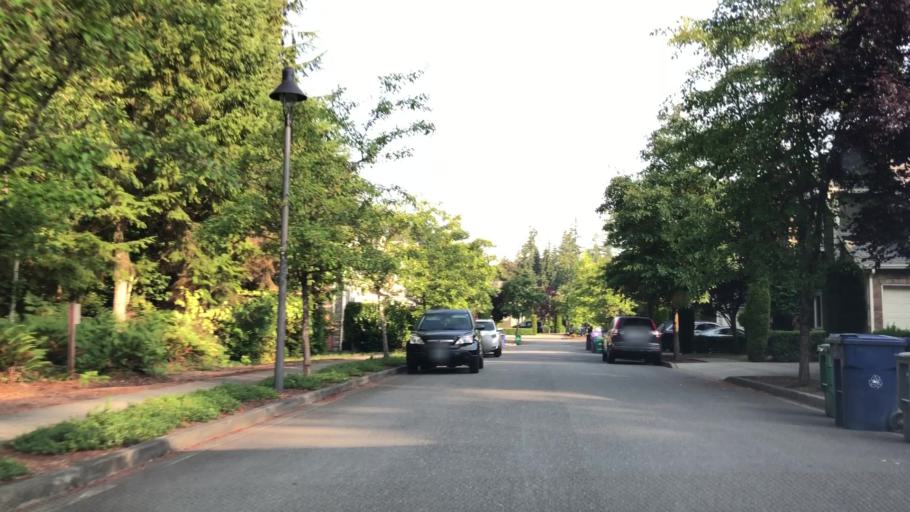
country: US
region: Washington
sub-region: King County
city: Union Hill-Novelty Hill
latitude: 47.6757
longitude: -122.0276
